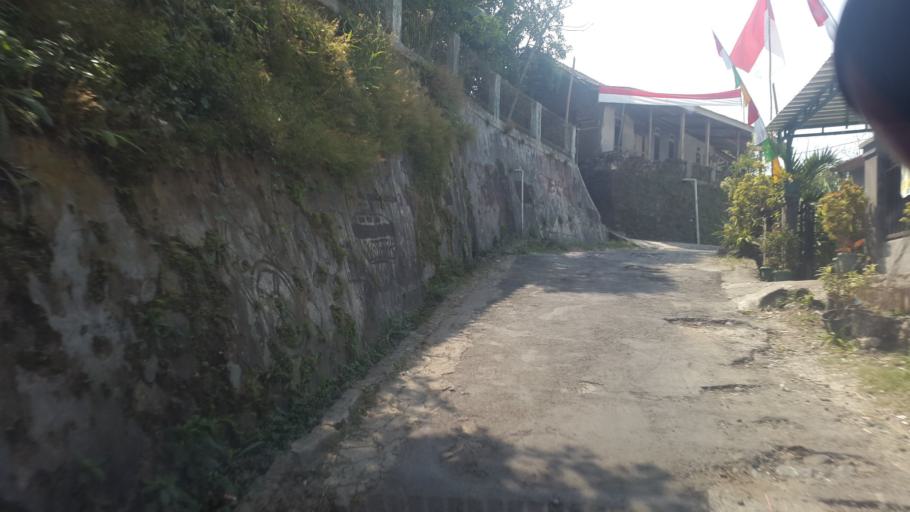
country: ID
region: West Java
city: Cicurug
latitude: -6.7673
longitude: 106.7598
